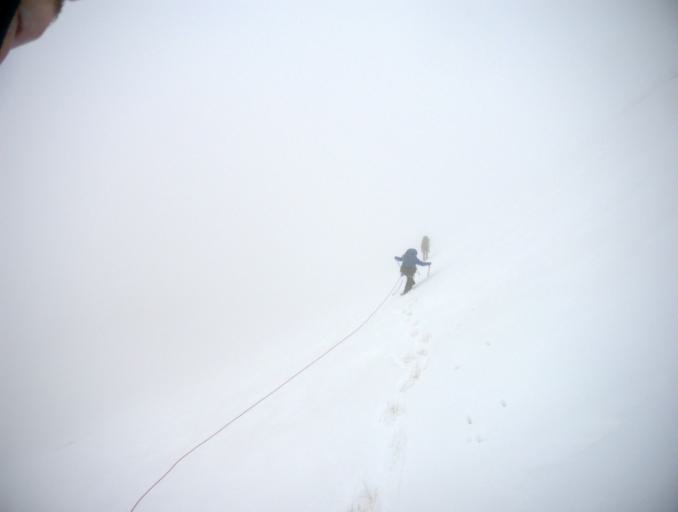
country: RU
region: Kabardino-Balkariya
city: Terskol
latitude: 43.3804
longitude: 42.4674
